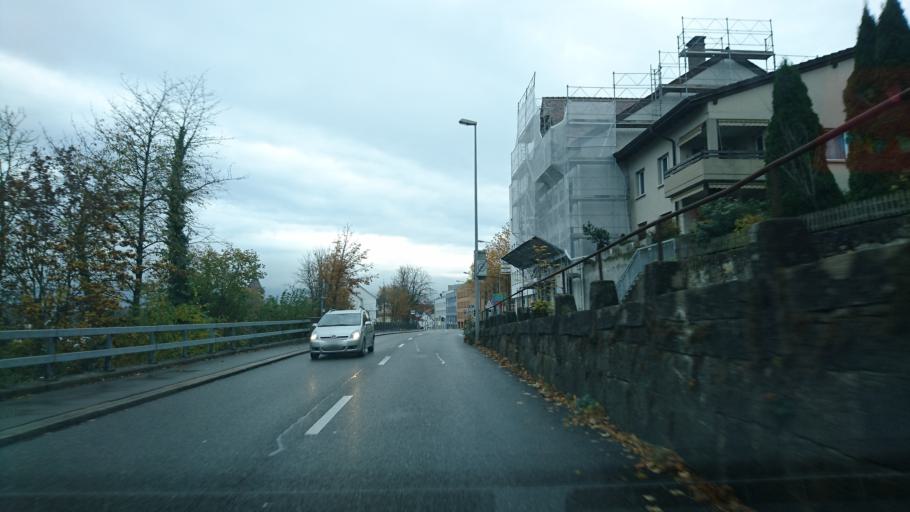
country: CH
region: Aargau
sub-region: Bezirk Aarau
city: Aarau
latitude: 47.3884
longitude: 8.0412
